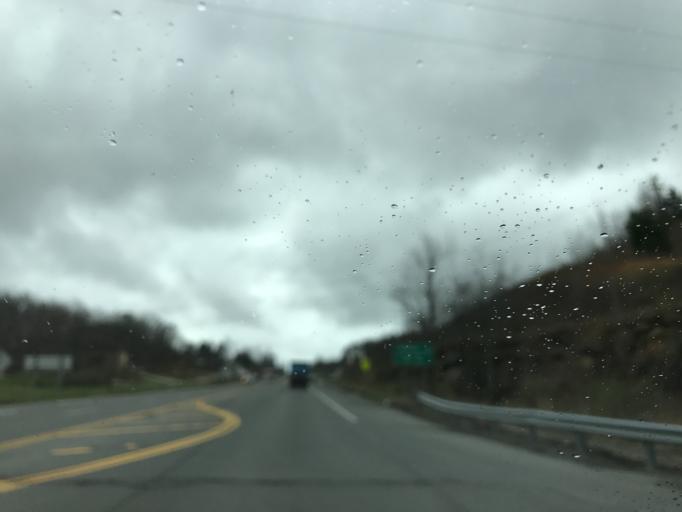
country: US
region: West Virginia
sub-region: Raleigh County
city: Prosperity
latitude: 37.8504
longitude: -81.1966
